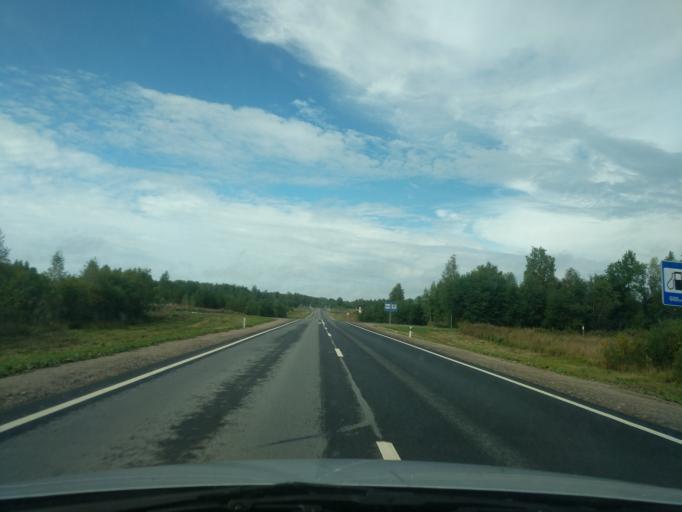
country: RU
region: Kostroma
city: Sudislavl'
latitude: 57.8271
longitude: 41.8920
